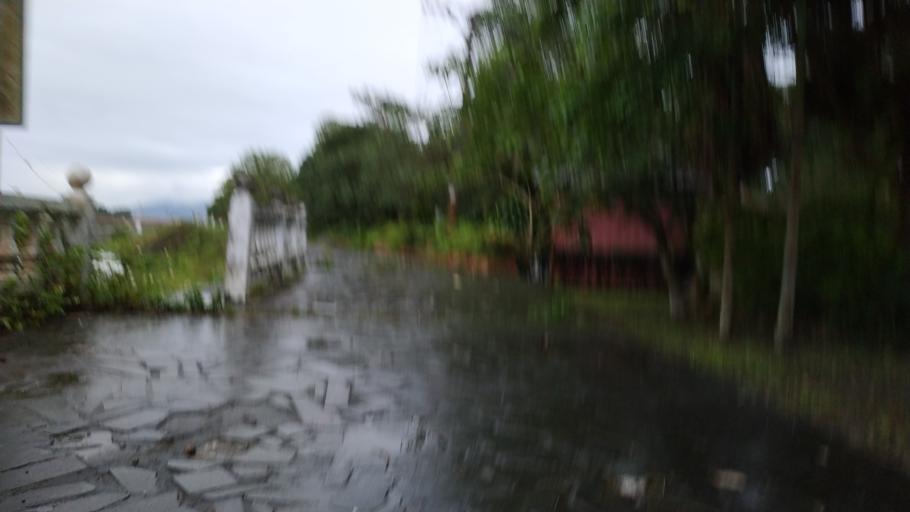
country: TW
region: Taiwan
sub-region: Hualien
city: Hualian
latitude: 23.6602
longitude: 121.4212
